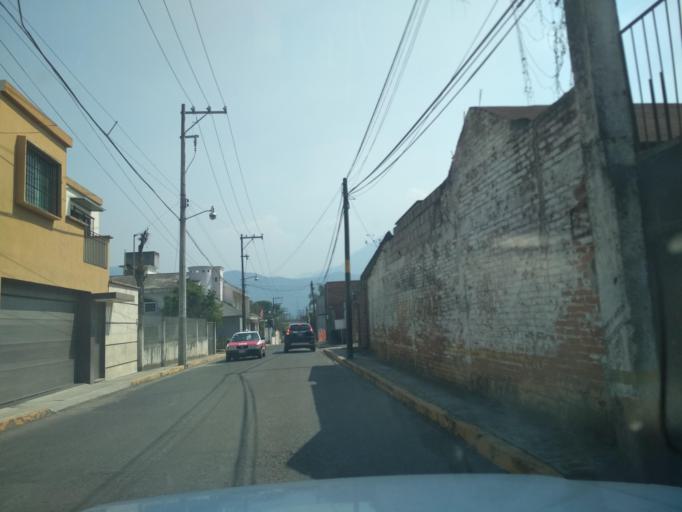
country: MX
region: Veracruz
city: Orizaba
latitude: 18.8426
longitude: -97.0856
